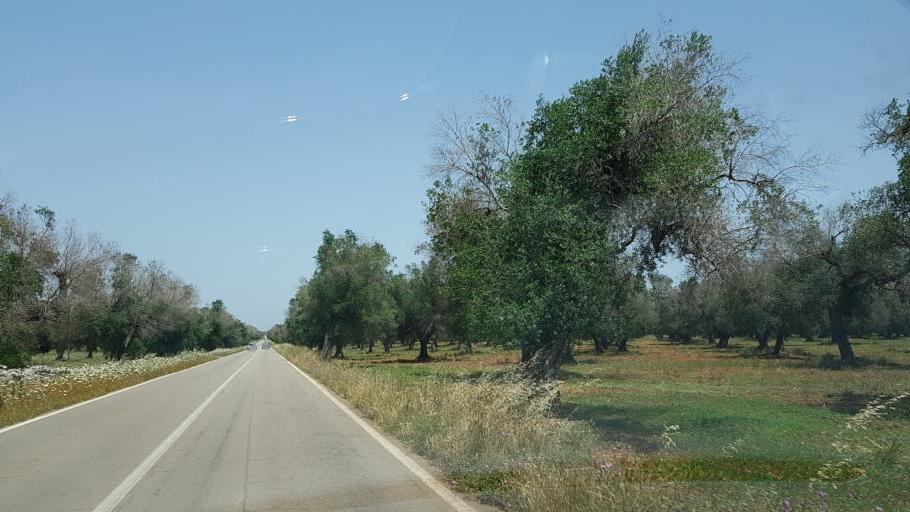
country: IT
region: Apulia
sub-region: Provincia di Lecce
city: Veglie
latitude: 40.3099
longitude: 17.9201
